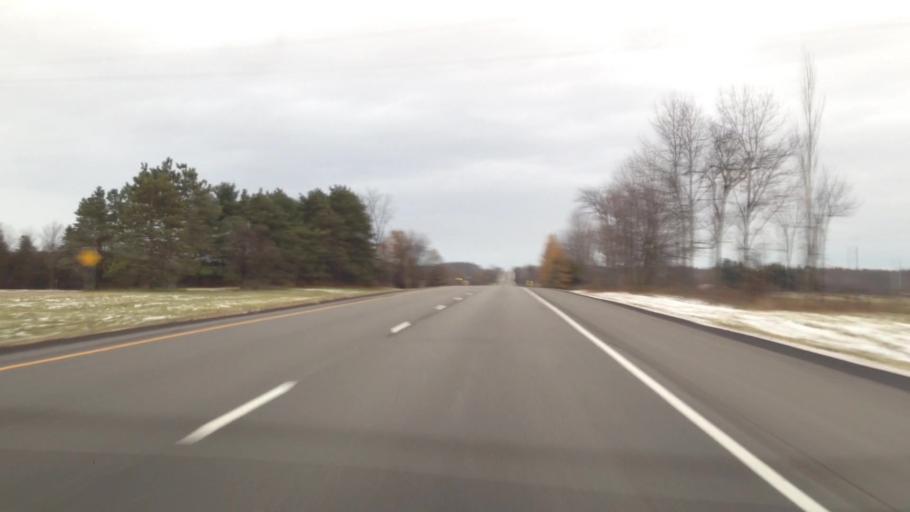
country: CA
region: Quebec
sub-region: Laurentides
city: Brownsburg-Chatham
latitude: 45.5472
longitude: -74.4231
